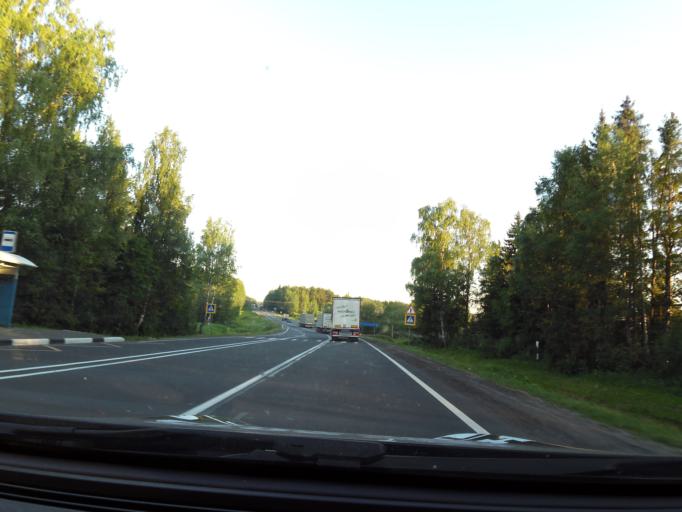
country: RU
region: Jaroslavl
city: Prechistoye
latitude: 58.4496
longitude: 40.3209
